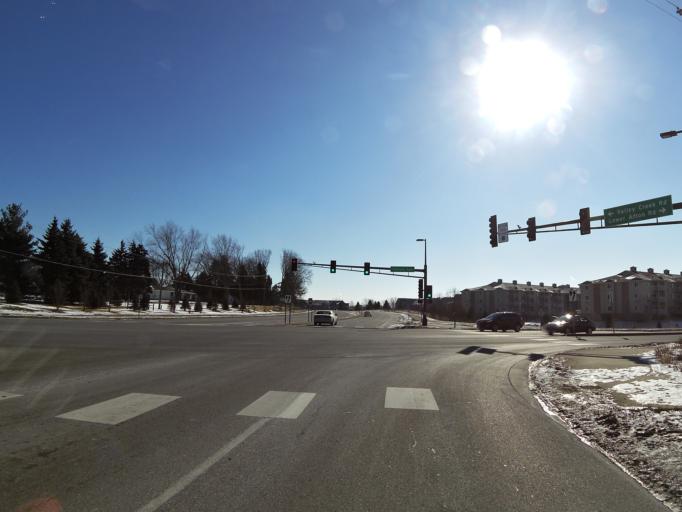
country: US
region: Minnesota
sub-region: Washington County
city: Woodbury
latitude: 44.9280
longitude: -92.9849
